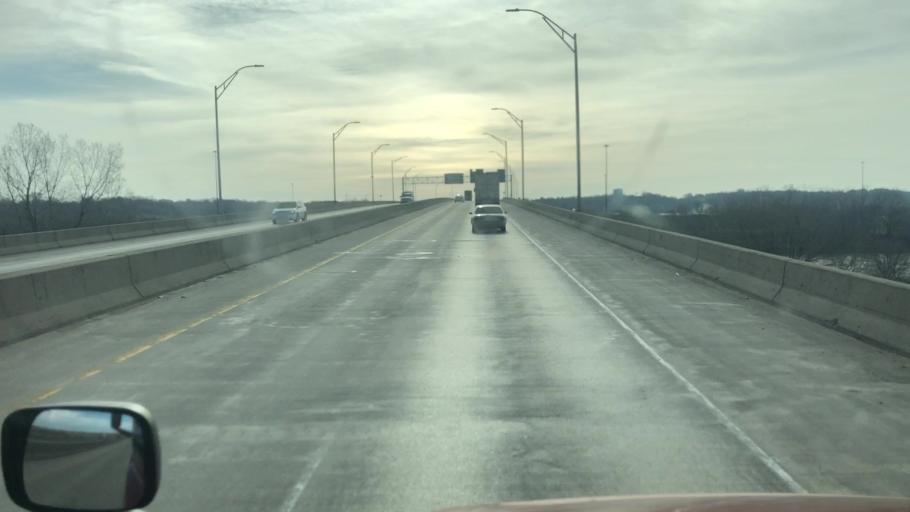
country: US
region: Nebraska
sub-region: Dakota County
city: South Sioux City
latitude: 42.4472
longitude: -96.3836
